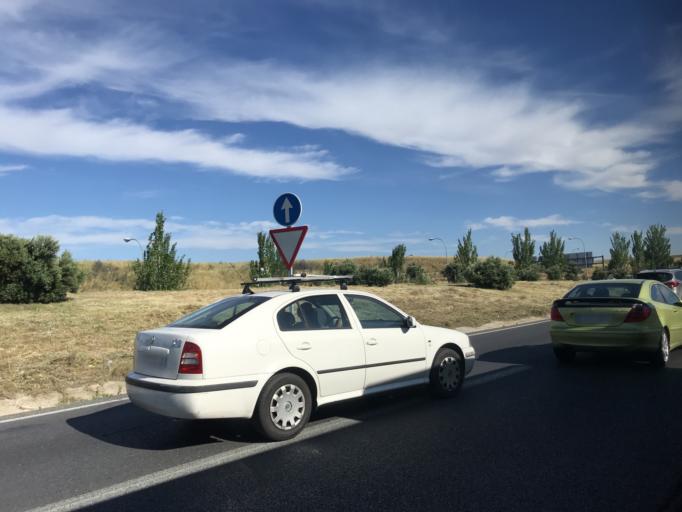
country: ES
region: Madrid
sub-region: Provincia de Madrid
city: San Blas
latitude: 40.4387
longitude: -3.5939
